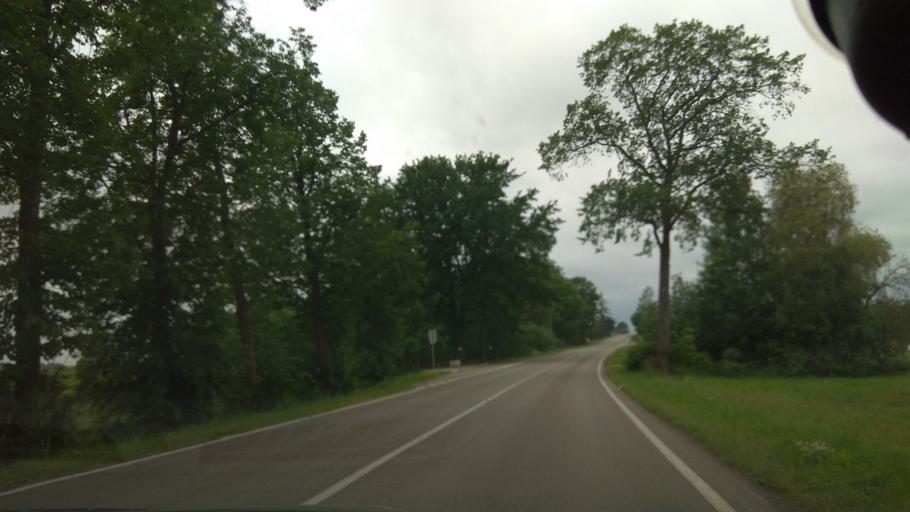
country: LT
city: Linkuva
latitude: 56.0826
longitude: 23.9077
